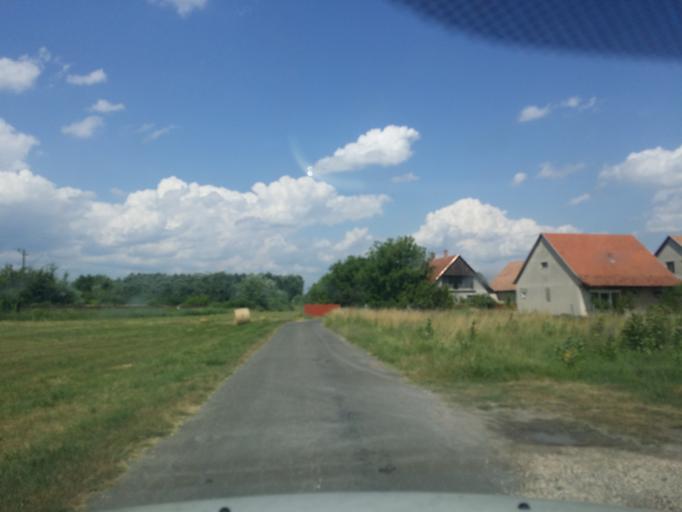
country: HU
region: Bacs-Kiskun
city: Jaszszentlaszlo
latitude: 46.5711
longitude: 19.7638
